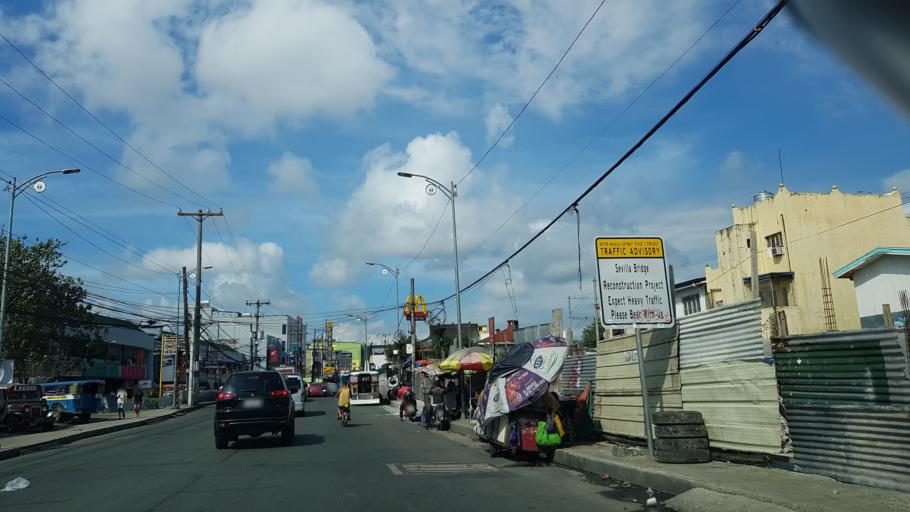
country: PH
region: Metro Manila
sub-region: San Juan
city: San Juan
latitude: 14.5887
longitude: 121.0221
